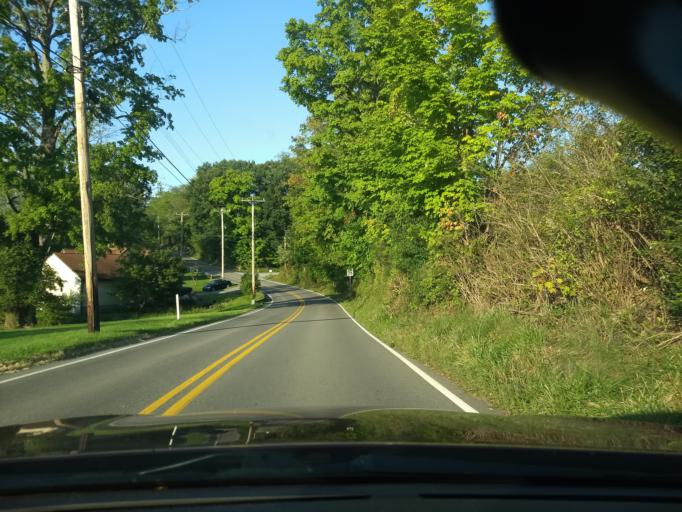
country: US
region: Pennsylvania
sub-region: Allegheny County
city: Gibsonia
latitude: 40.6314
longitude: -79.9658
